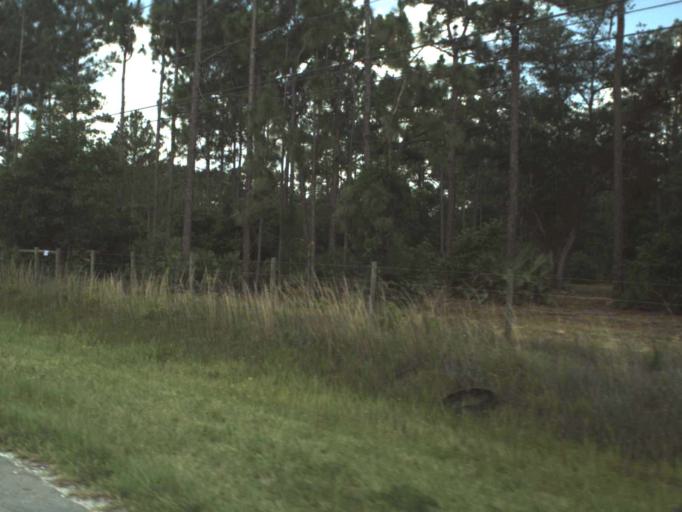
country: US
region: Florida
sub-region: Volusia County
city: Samsula-Spruce Creek
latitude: 28.9518
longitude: -81.0965
